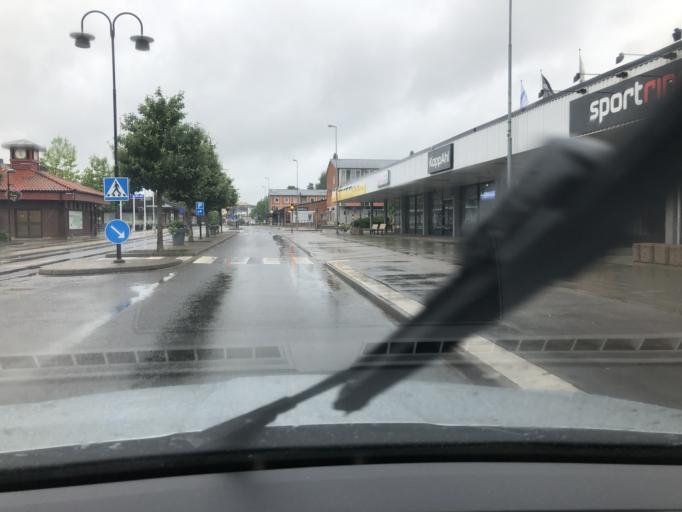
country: SE
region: Blekinge
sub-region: Olofstroms Kommun
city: Olofstroem
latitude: 56.2778
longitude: 14.5321
